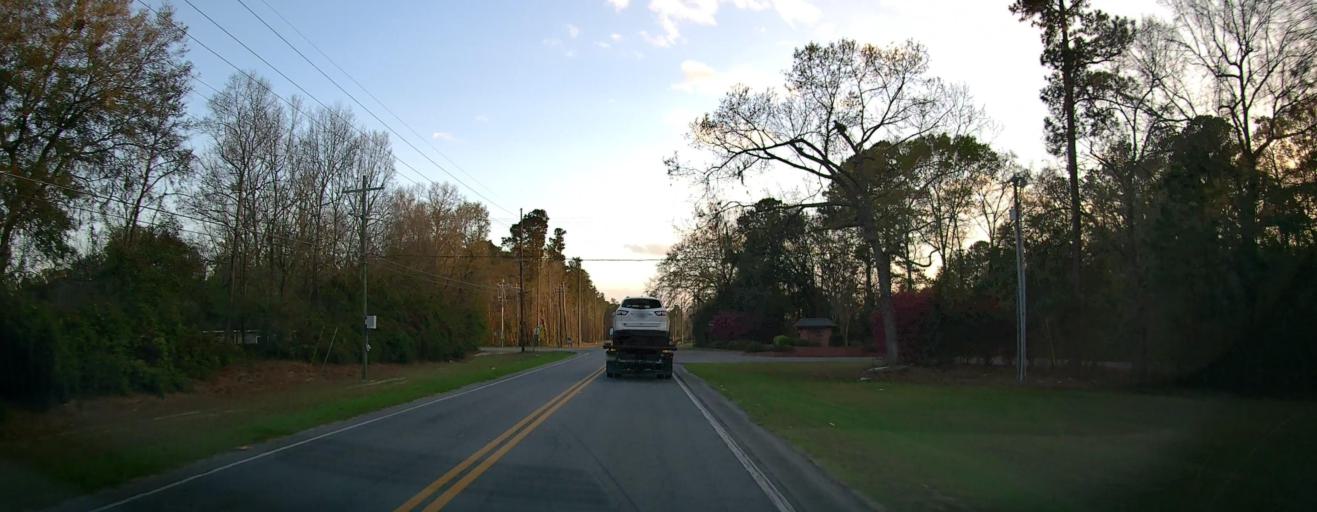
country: US
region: Georgia
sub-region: Chatham County
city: Bloomingdale
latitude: 32.1531
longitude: -81.3882
